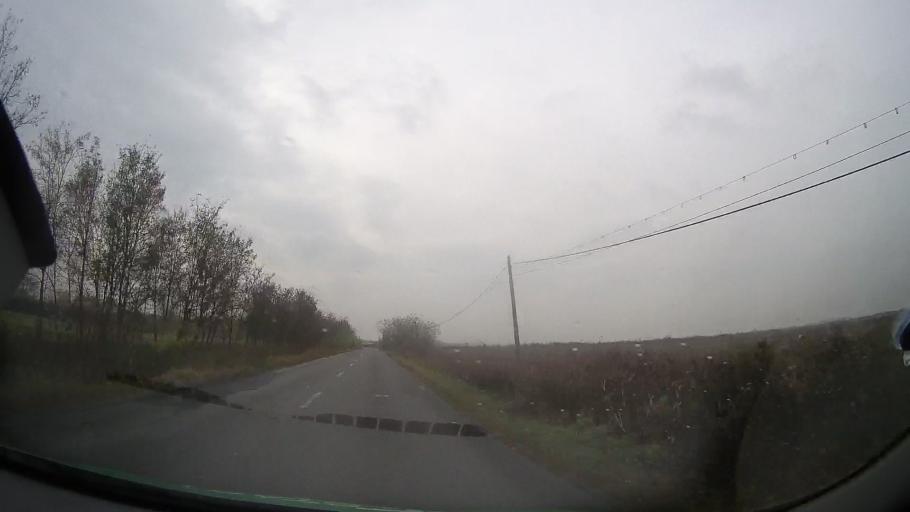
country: RO
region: Prahova
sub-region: Comuna Gherghita
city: Gherghita
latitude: 44.8199
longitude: 26.2724
